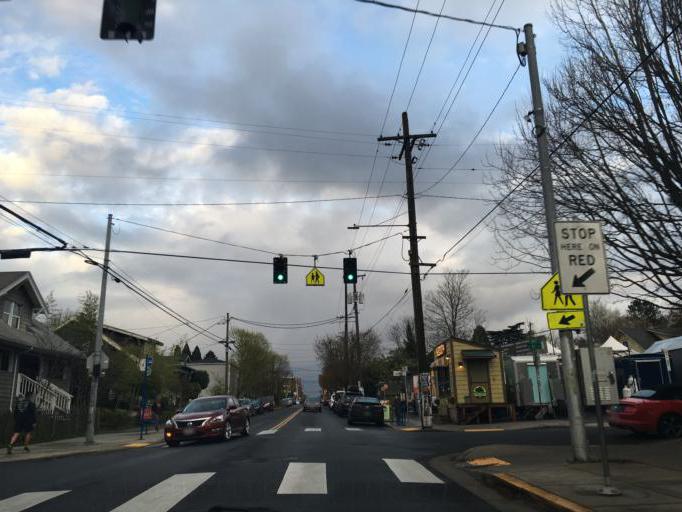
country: US
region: Oregon
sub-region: Multnomah County
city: Portland
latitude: 45.5048
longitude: -122.6369
